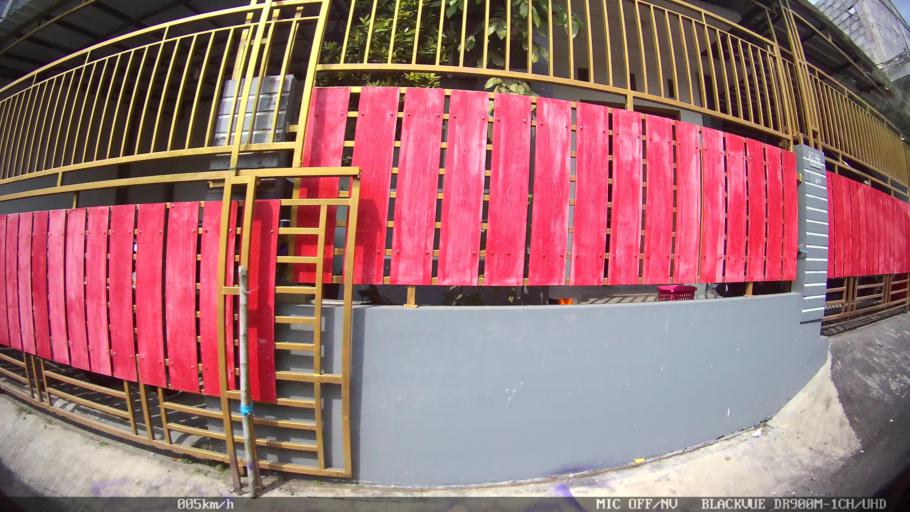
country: ID
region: Daerah Istimewa Yogyakarta
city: Yogyakarta
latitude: -7.7635
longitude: 110.3563
